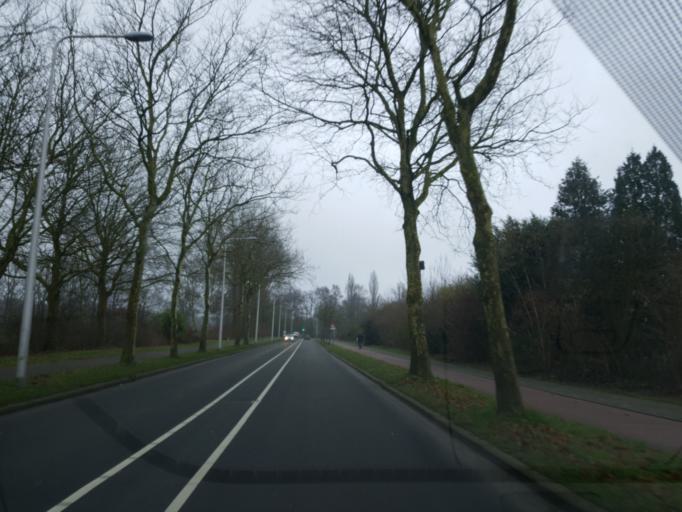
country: NL
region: North Holland
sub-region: Gemeente Bussum
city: Bussum
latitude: 52.2705
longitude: 5.1407
